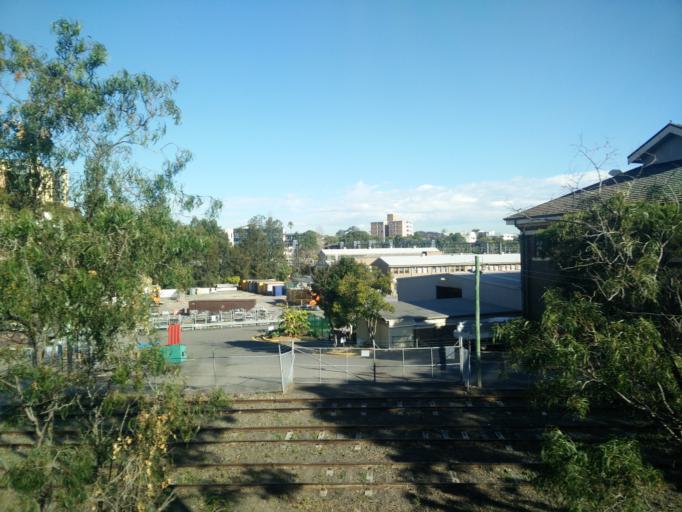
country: AU
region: New South Wales
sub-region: Strathfield
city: Homebush
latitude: -33.8677
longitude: 151.0910
